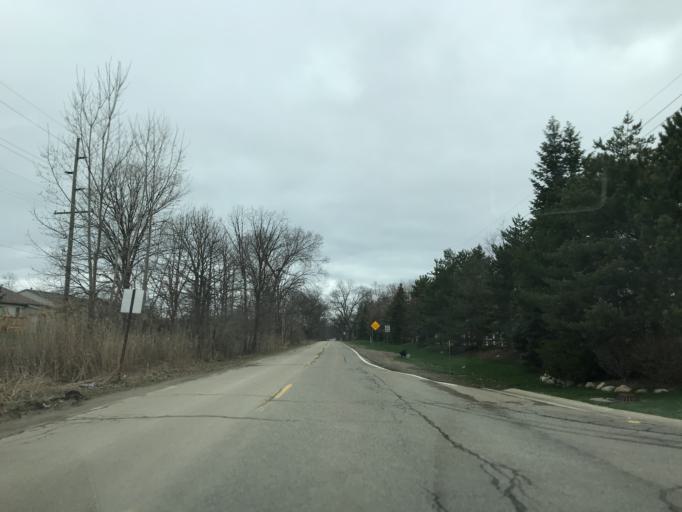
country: US
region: Michigan
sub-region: Oakland County
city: South Lyon
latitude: 42.4748
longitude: -83.6606
